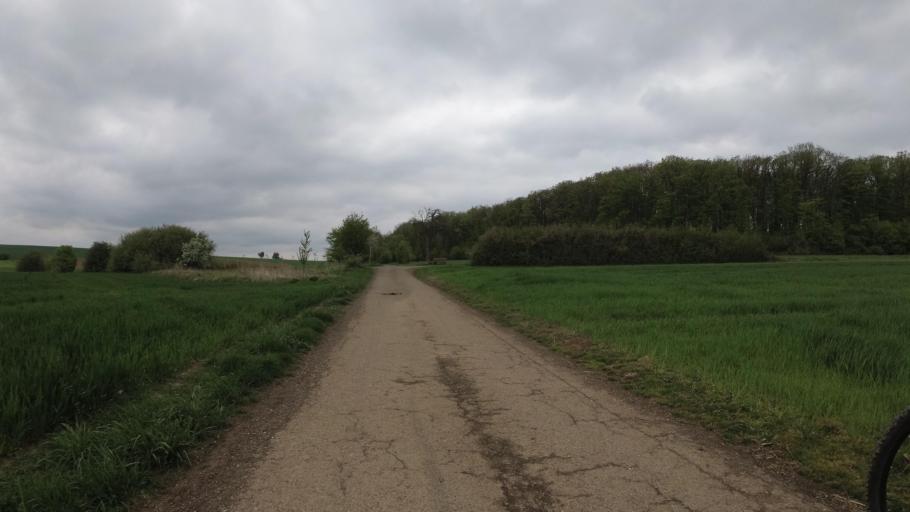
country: DE
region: Saarland
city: Merzig
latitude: 49.4045
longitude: 6.5704
